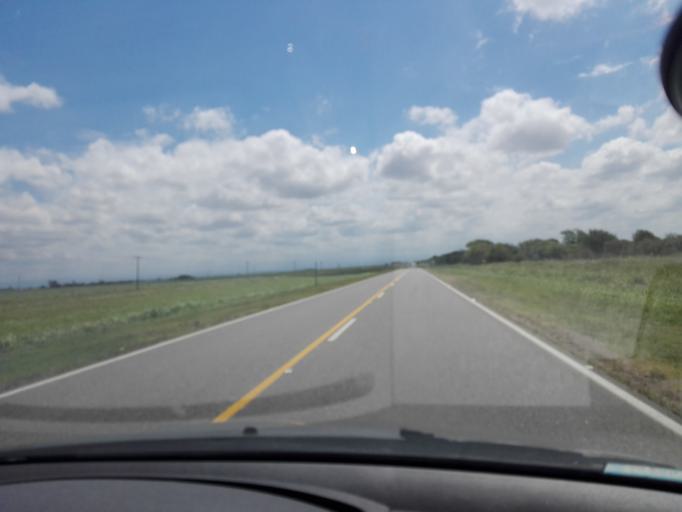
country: AR
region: Cordoba
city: Toledo
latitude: -31.6485
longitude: -64.1081
